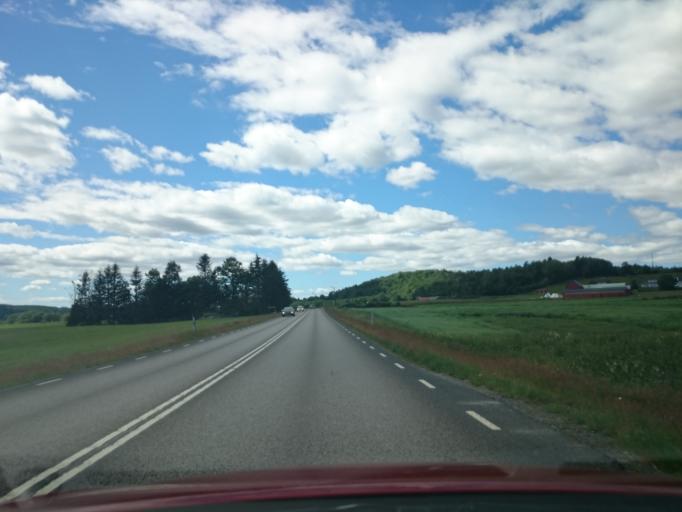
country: SE
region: Vaestra Goetaland
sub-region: Lerums Kommun
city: Olstorp
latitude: 57.8240
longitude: 12.2124
